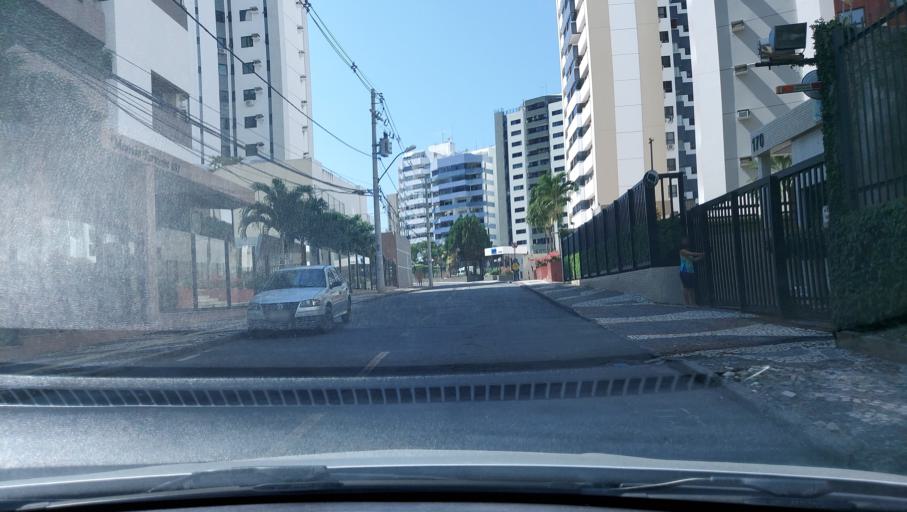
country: BR
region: Bahia
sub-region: Salvador
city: Salvador
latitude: -12.9876
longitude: -38.4630
